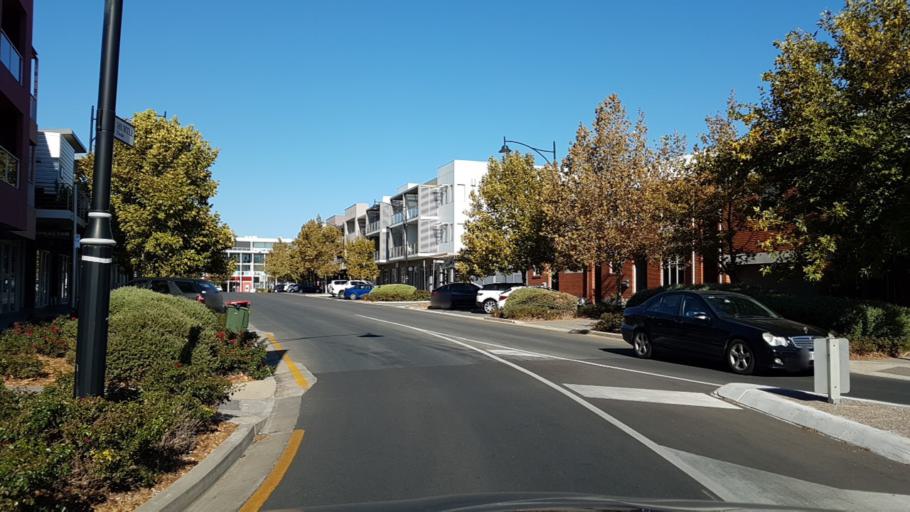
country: AU
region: South Australia
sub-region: Salisbury
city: Ingle Farm
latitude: -34.8080
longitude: 138.6149
